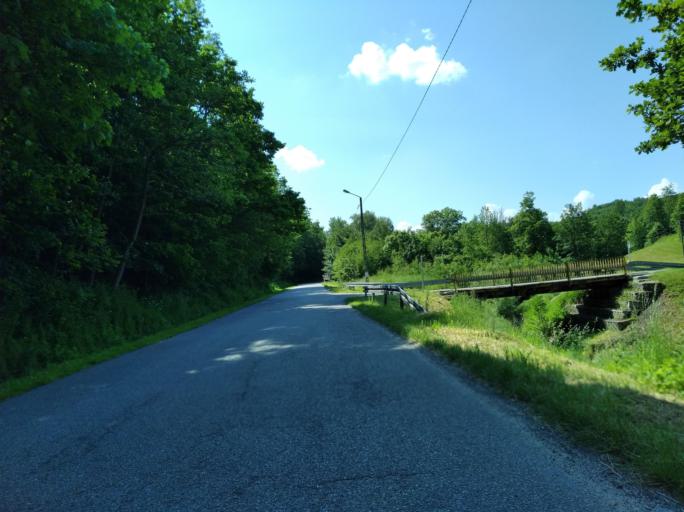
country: PL
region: Subcarpathian Voivodeship
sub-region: Powiat ropczycko-sedziszowski
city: Zagorzyce
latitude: 49.9887
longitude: 21.6454
